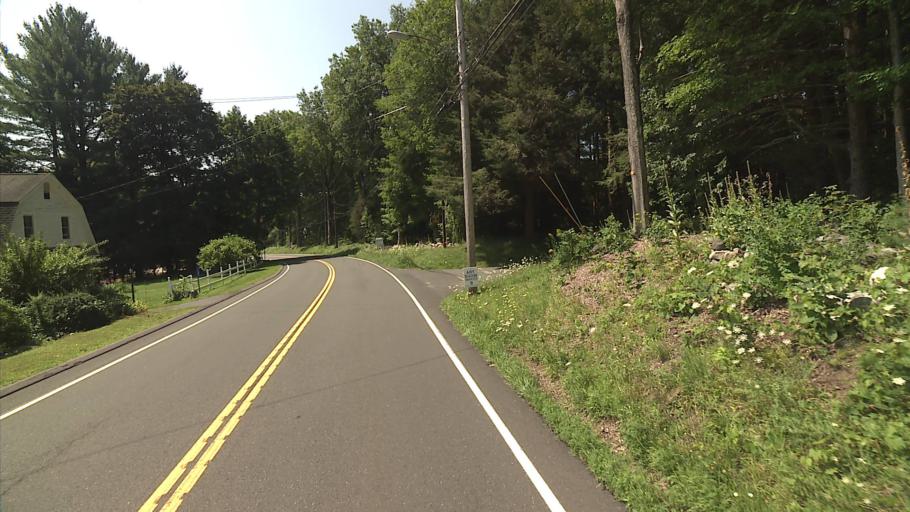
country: US
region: Connecticut
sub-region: Litchfield County
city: Winchester Center
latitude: 41.9973
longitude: -73.2031
